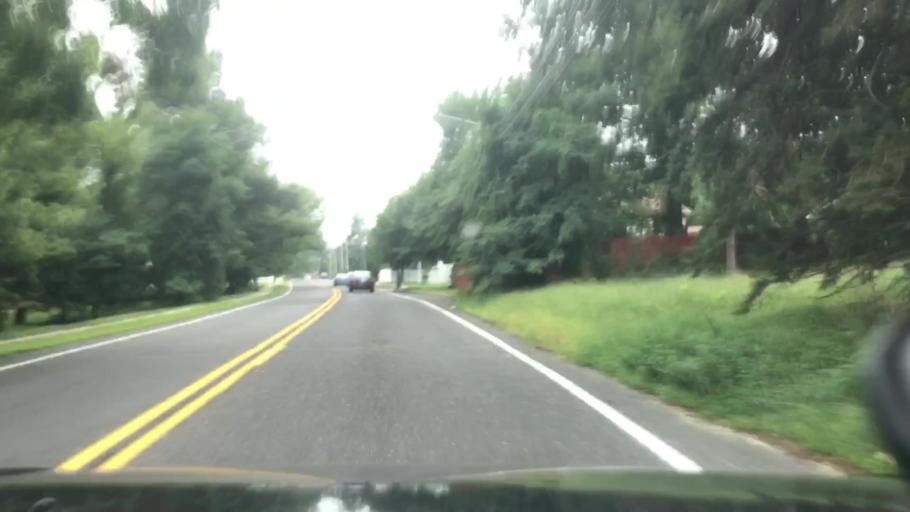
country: US
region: New Jersey
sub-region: Monmouth County
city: Eatontown
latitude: 40.2873
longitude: -74.0473
